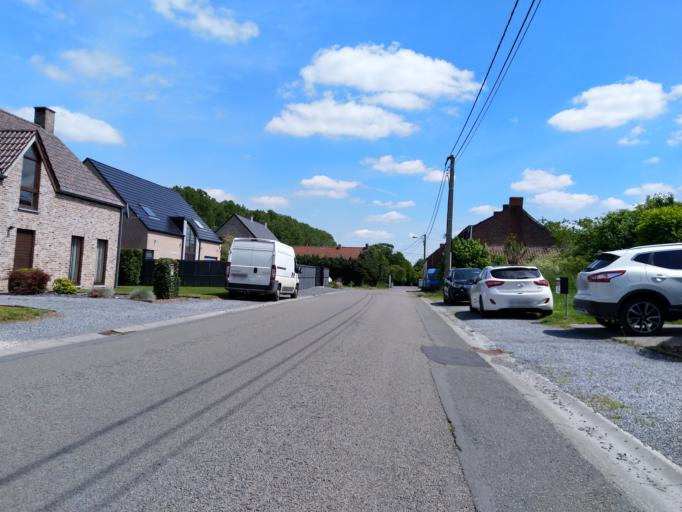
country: BE
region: Wallonia
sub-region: Province du Hainaut
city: Mons
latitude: 50.5147
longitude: 3.9913
